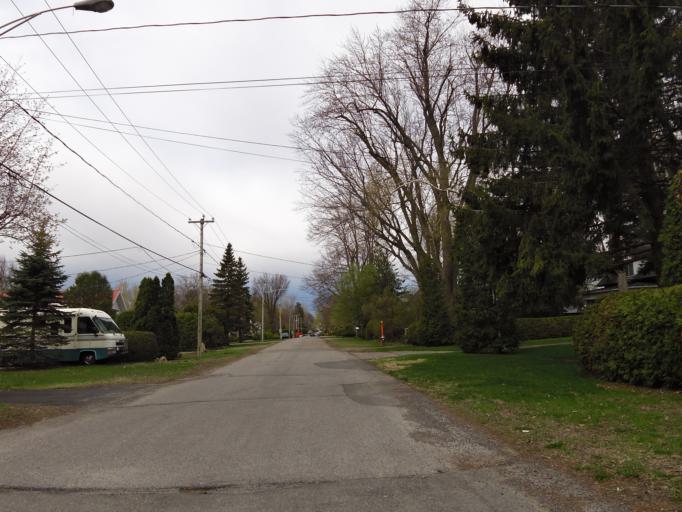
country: CA
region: Quebec
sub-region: Laurentides
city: Oka
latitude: 45.4629
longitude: -74.0815
